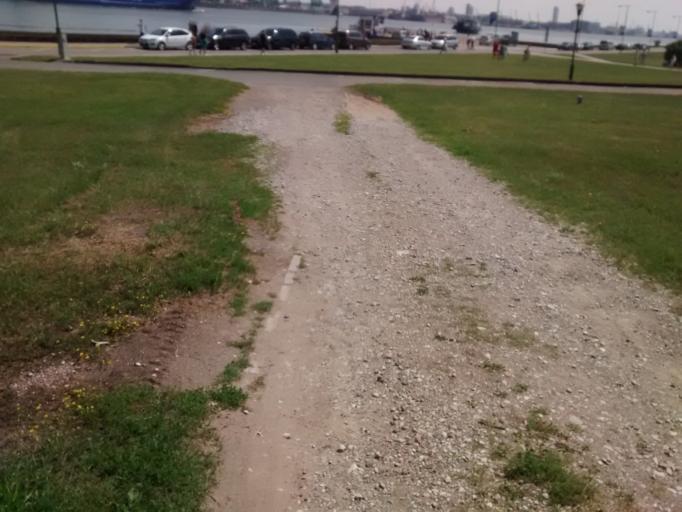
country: LT
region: Klaipedos apskritis
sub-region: Klaipeda
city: Klaipeda
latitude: 55.7159
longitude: 21.1024
